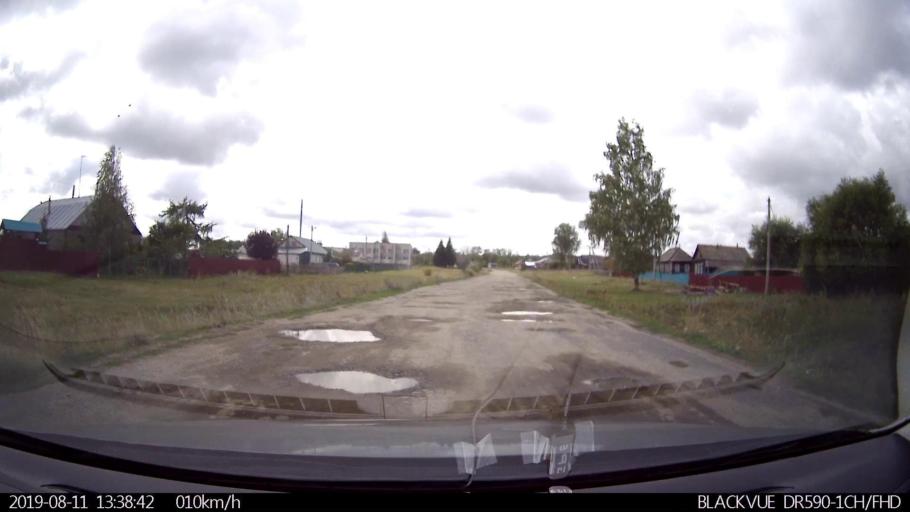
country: RU
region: Ulyanovsk
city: Ignatovka
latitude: 53.8596
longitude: 47.5812
